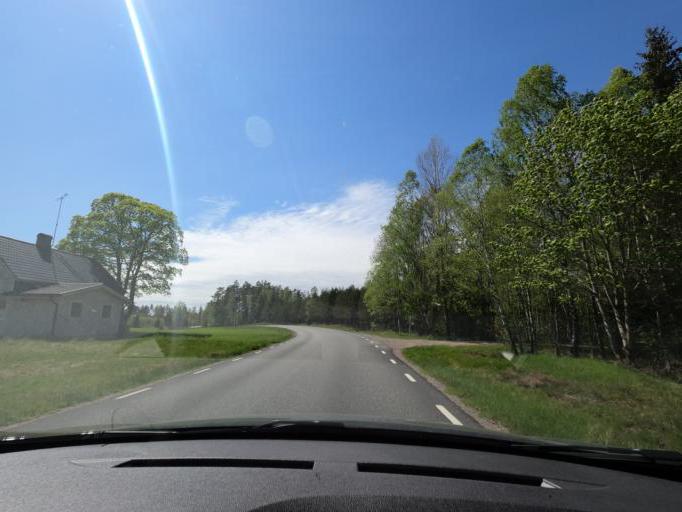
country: SE
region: Joenkoeping
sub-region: Varnamo Kommun
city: Bredaryd
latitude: 57.1536
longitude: 13.7327
